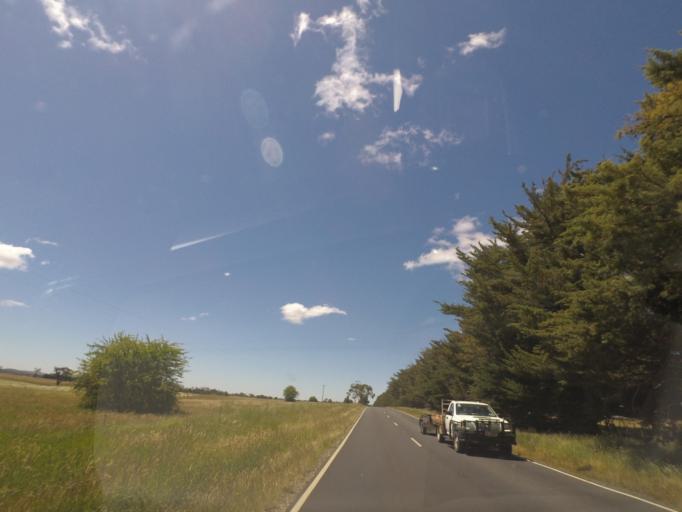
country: AU
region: Victoria
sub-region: Mount Alexander
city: Castlemaine
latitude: -37.2479
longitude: 144.3216
